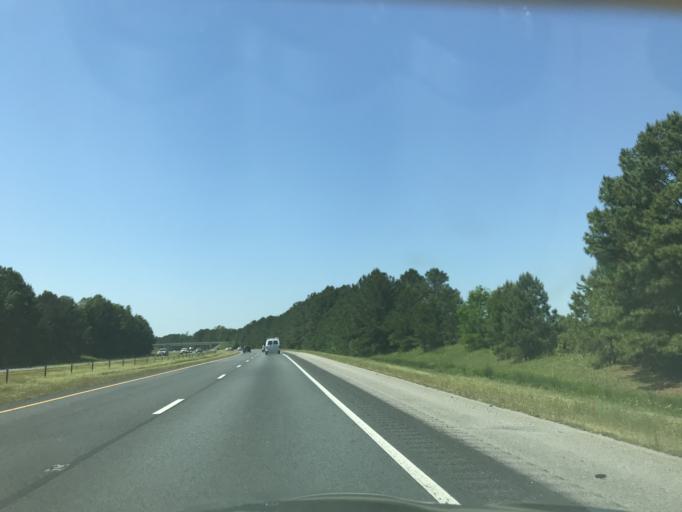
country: US
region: North Carolina
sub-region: Johnston County
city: Benson
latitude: 35.3375
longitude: -78.4620
